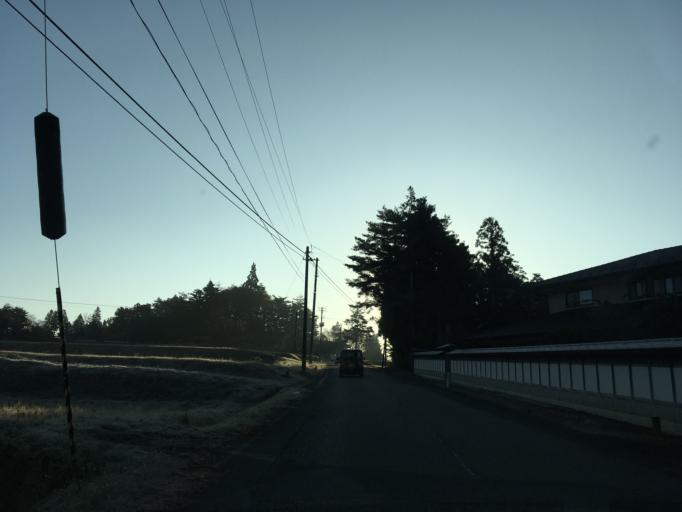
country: JP
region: Iwate
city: Ichinoseki
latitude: 38.7989
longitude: 141.2049
